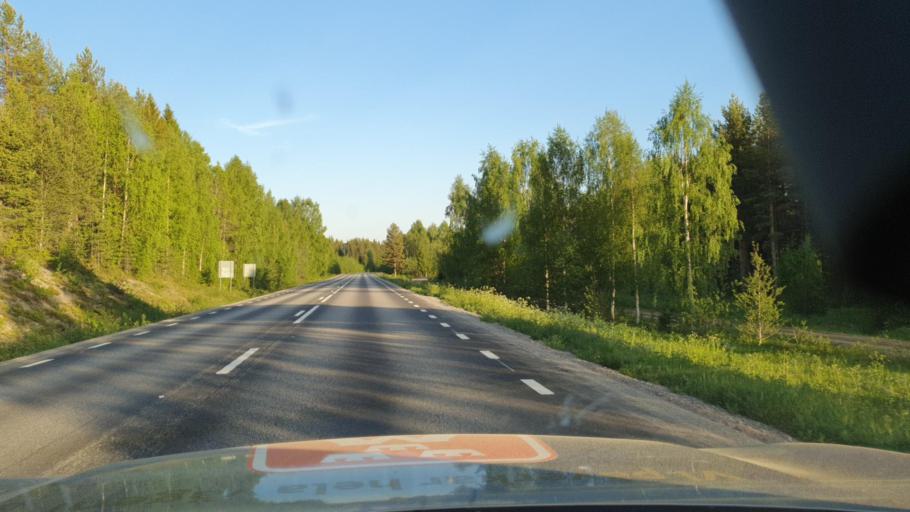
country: SE
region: Vaesternorrland
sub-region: Solleftea Kommun
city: As
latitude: 63.5741
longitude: 16.8321
